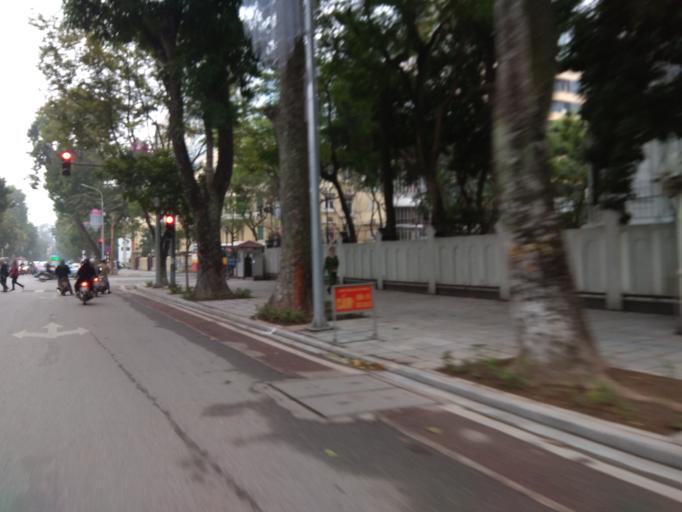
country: VN
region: Ha Noi
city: Hoan Kiem
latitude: 21.0222
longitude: 105.8562
